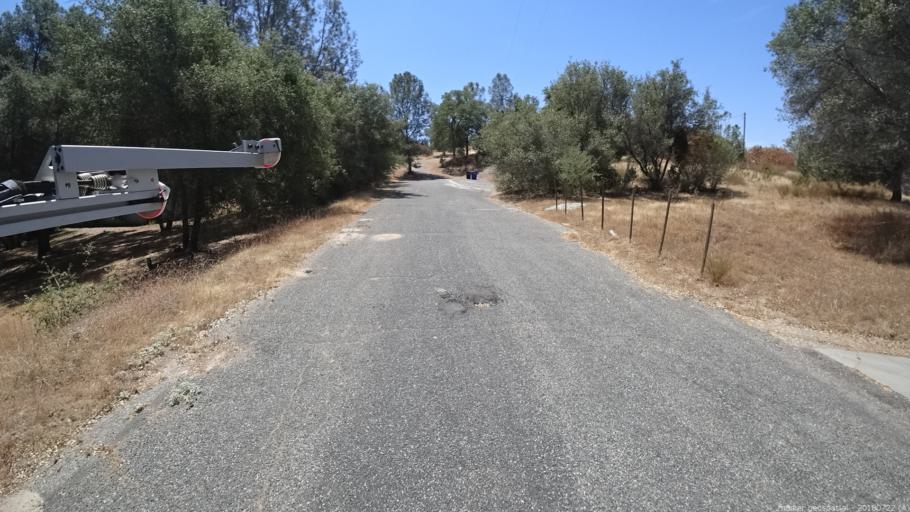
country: US
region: California
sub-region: Madera County
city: Coarsegold
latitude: 37.2775
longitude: -119.7586
